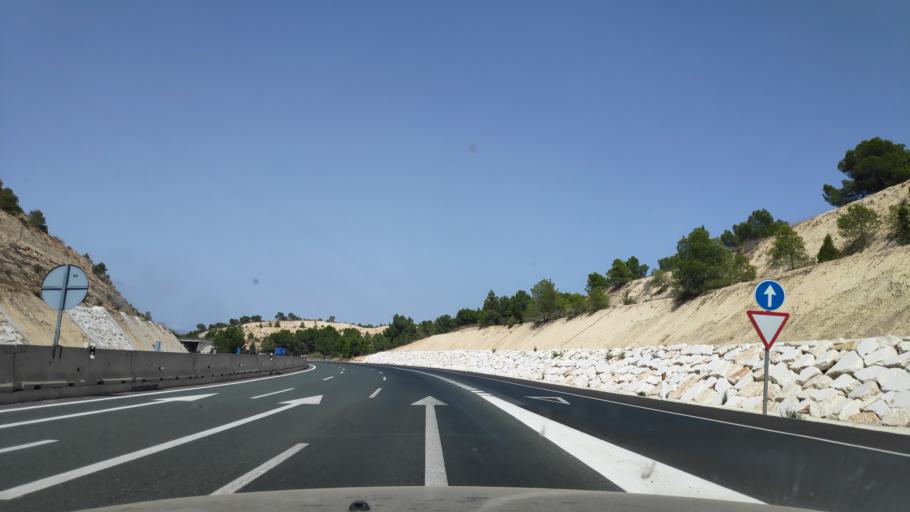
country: ES
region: Murcia
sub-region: Murcia
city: Murcia
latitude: 37.9215
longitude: -1.1585
